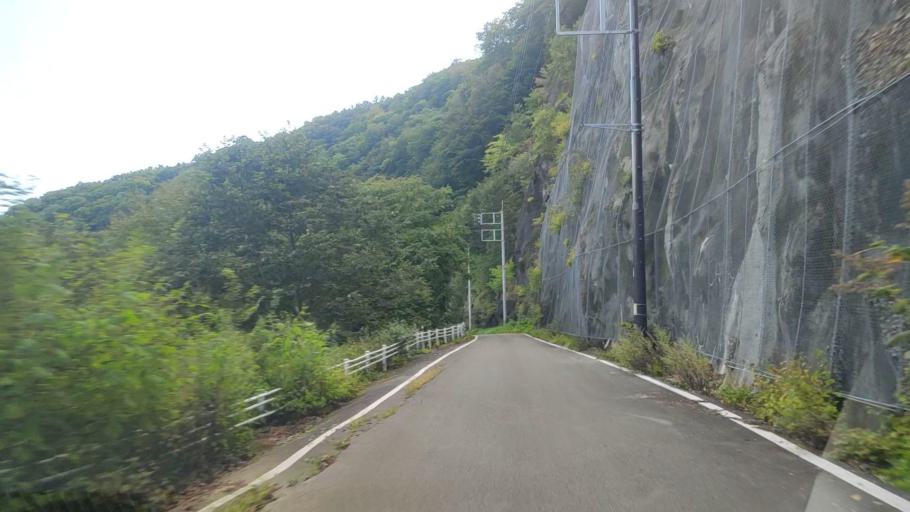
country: JP
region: Gunma
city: Nakanojomachi
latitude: 36.6508
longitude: 138.6199
